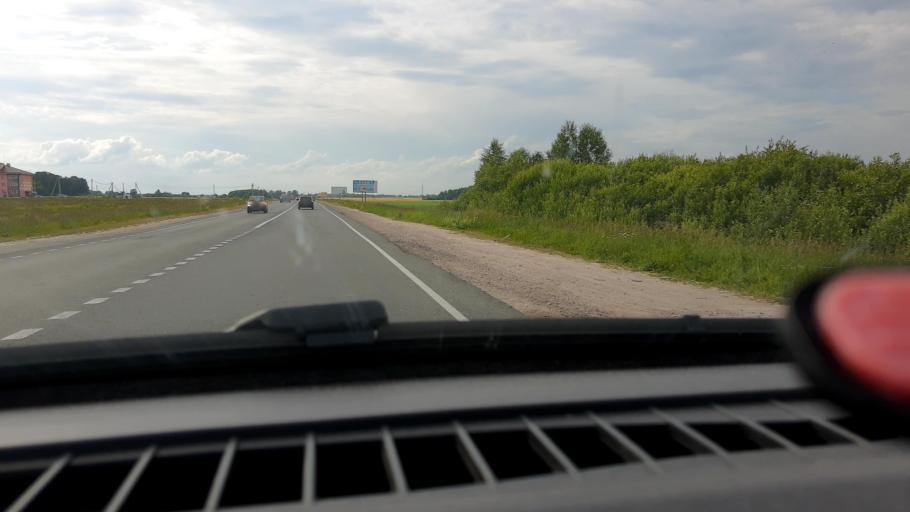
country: RU
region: Nizjnij Novgorod
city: Gorodets
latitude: 56.6708
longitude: 43.4844
